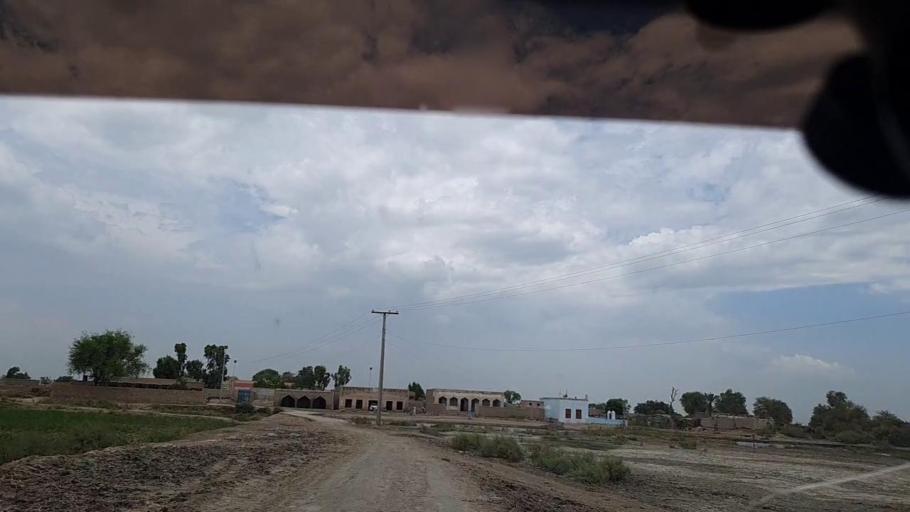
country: PK
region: Sindh
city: Ghauspur
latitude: 28.1152
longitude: 68.9883
